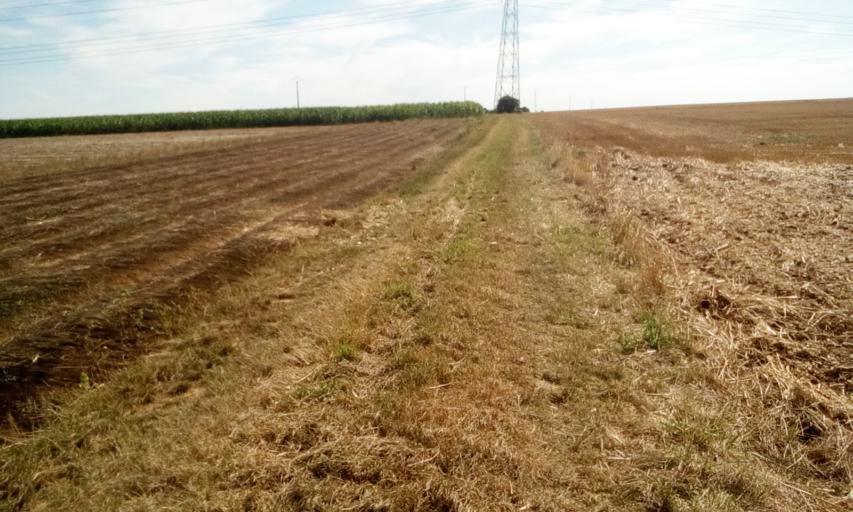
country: FR
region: Lower Normandy
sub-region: Departement du Calvados
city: Eterville
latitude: 49.1212
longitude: -0.4311
